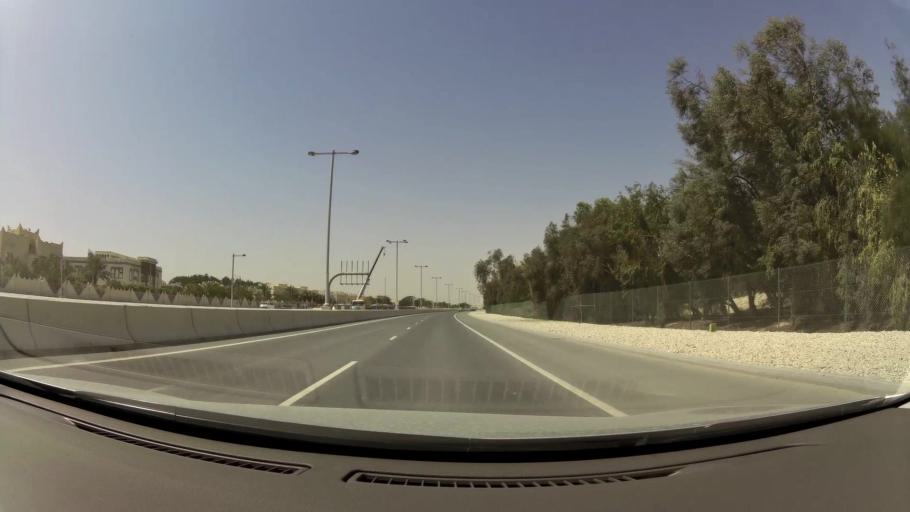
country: QA
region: Baladiyat ad Dawhah
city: Doha
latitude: 25.3796
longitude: 51.5157
